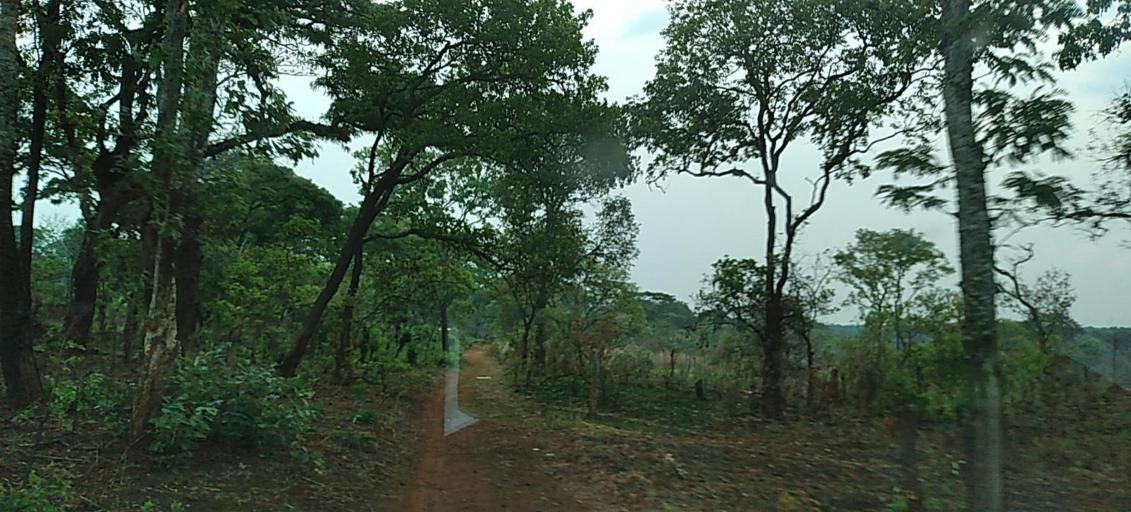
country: ZM
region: North-Western
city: Solwezi
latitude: -12.0450
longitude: 26.0091
